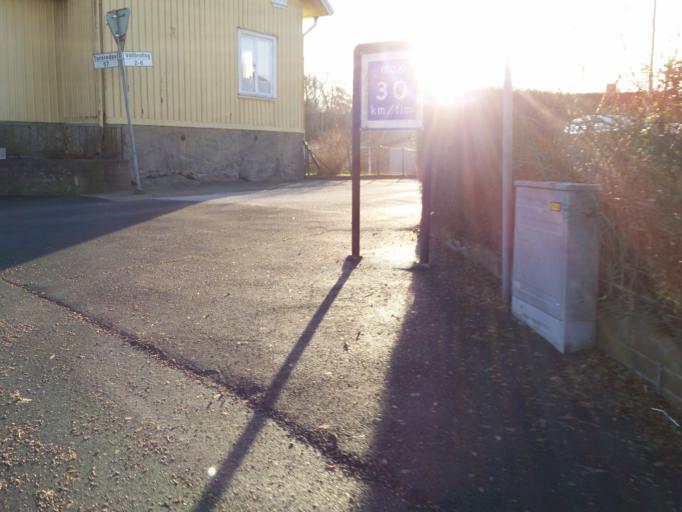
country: SE
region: Vaestra Goetaland
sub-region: Trollhattan
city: Trollhattan
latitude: 58.2826
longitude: 12.2651
